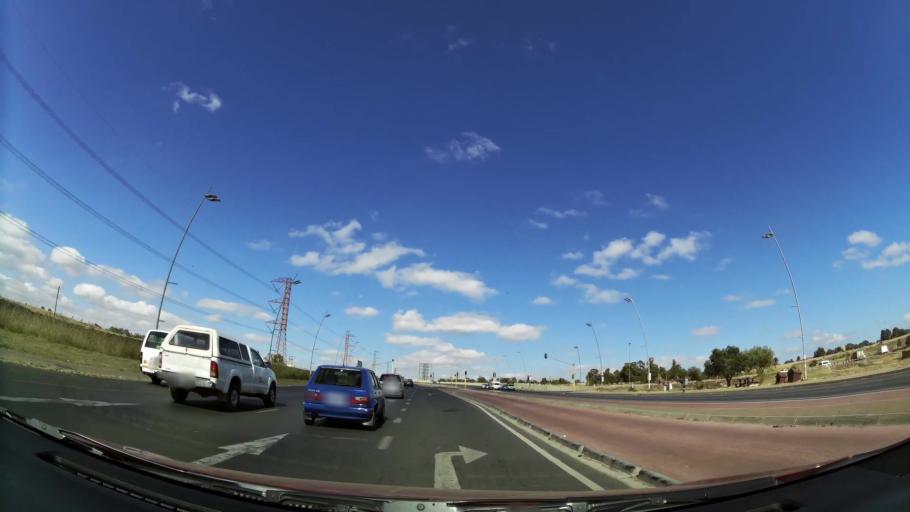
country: ZA
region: Gauteng
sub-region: City of Johannesburg Metropolitan Municipality
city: Modderfontein
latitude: -26.0547
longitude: 28.1835
